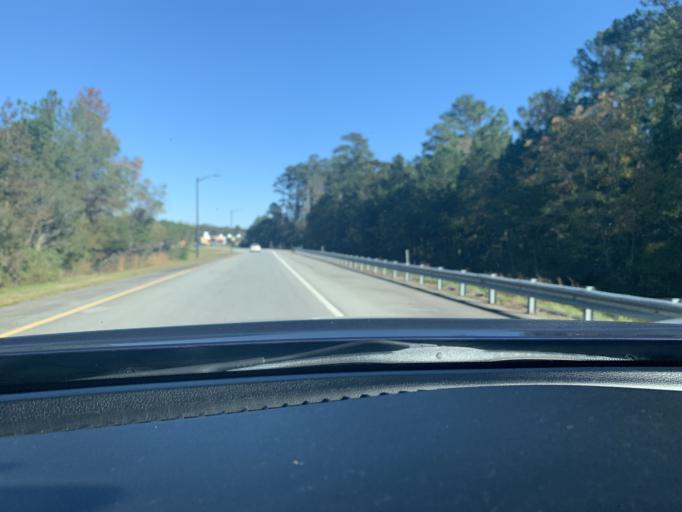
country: US
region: Georgia
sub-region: Chatham County
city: Pooler
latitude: 32.1181
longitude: -81.2672
